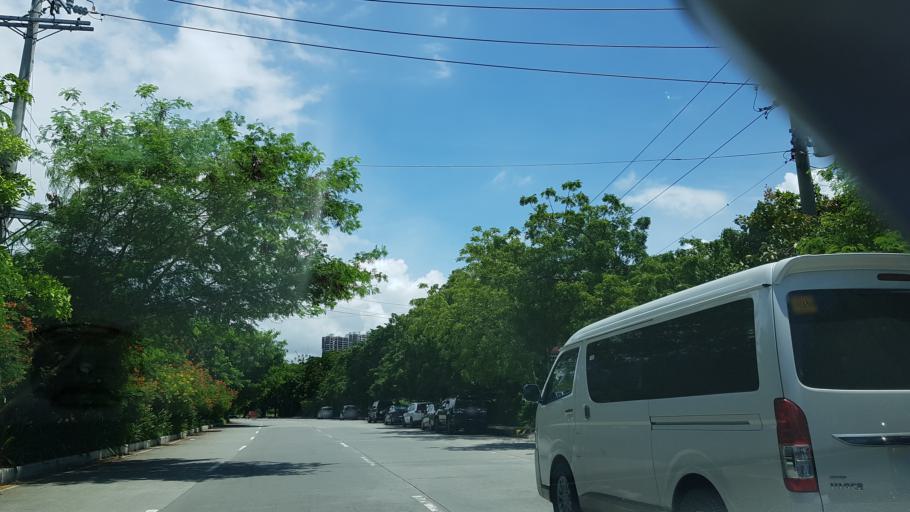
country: PH
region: Metro Manila
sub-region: City of Manila
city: Port Area
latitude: 14.5493
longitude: 120.9827
